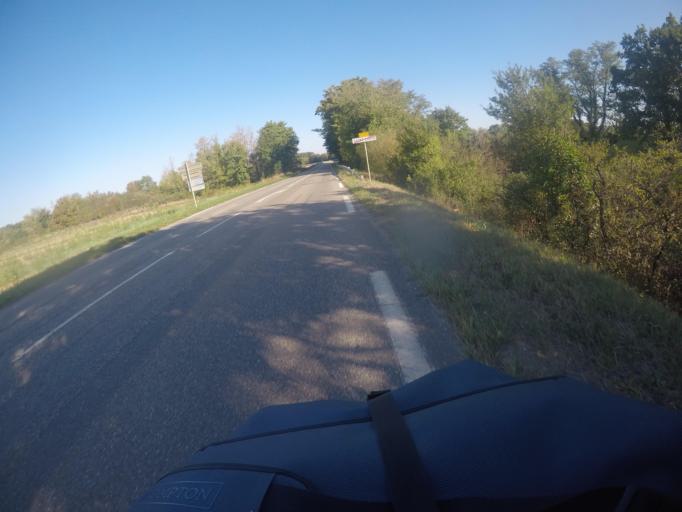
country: FR
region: Alsace
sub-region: Departement du Haut-Rhin
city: Rosenau
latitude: 47.6300
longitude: 7.5244
